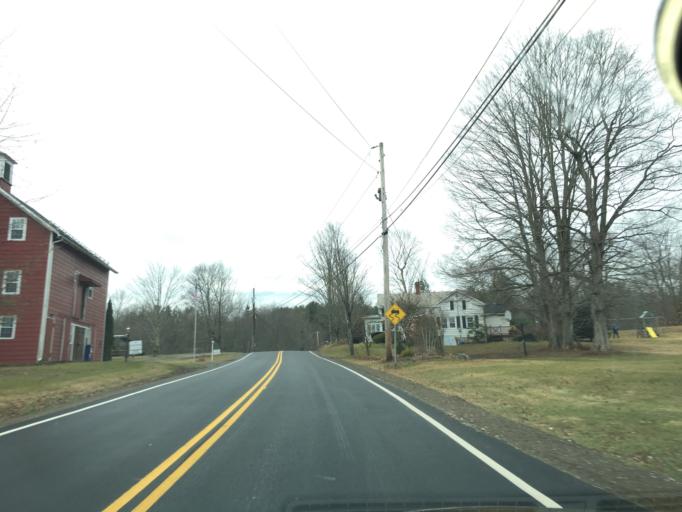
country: US
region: New York
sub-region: Rensselaer County
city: Averill Park
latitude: 42.6152
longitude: -73.5712
